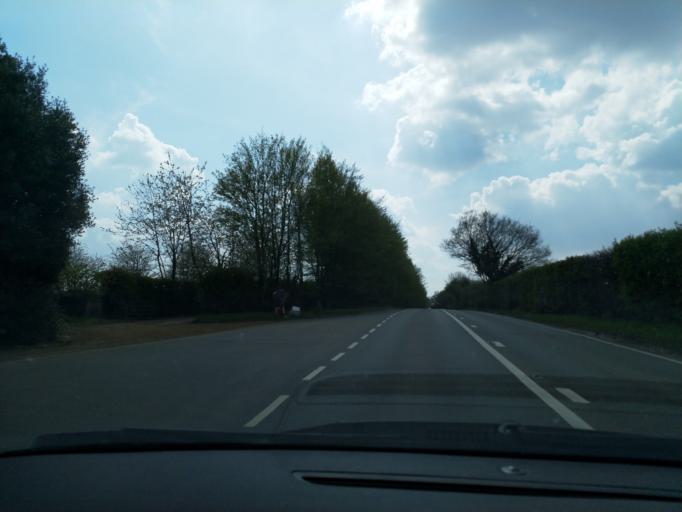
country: GB
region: England
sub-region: Warwickshire
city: Royal Leamington Spa
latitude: 52.3224
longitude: -1.5116
